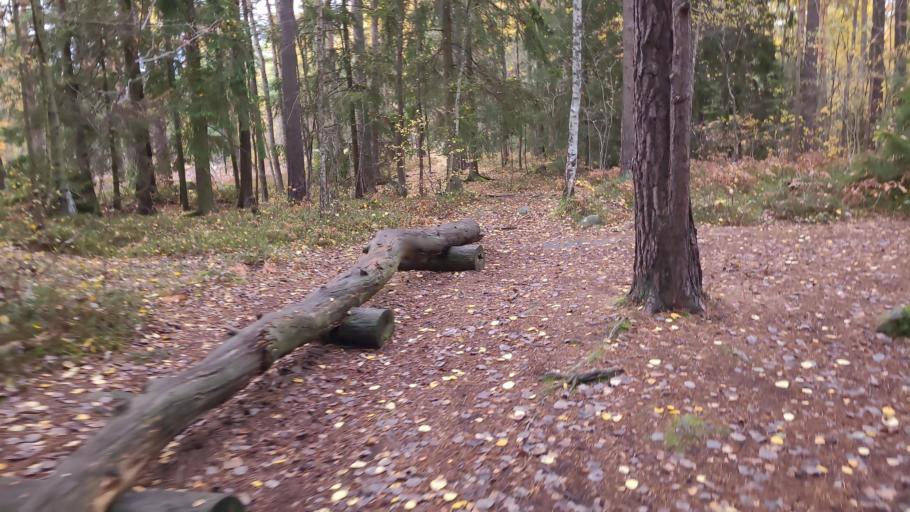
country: SE
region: Stockholm
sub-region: Solna Kommun
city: Rasunda
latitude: 59.3846
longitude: 17.9695
